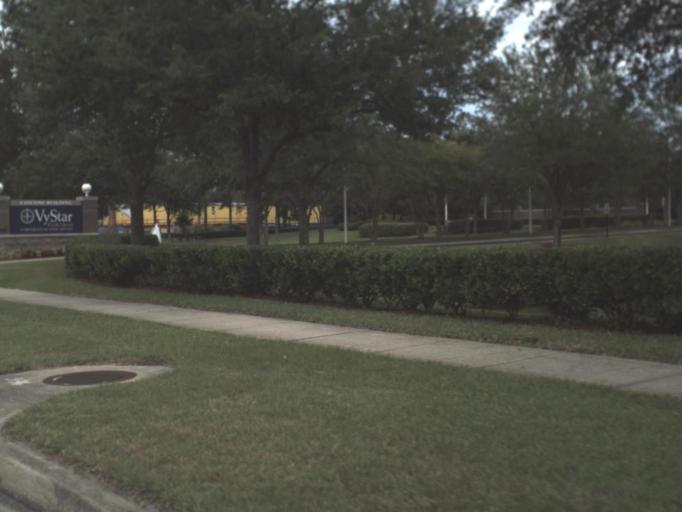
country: US
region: Florida
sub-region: Clay County
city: Bellair-Meadowbrook Terrace
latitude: 30.2528
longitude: -81.7430
